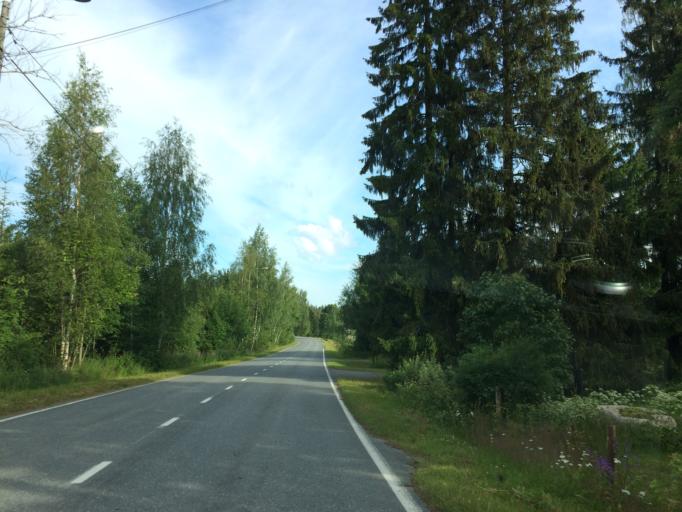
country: FI
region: Haeme
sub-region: Haemeenlinna
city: Janakkala
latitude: 60.9264
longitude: 24.5837
